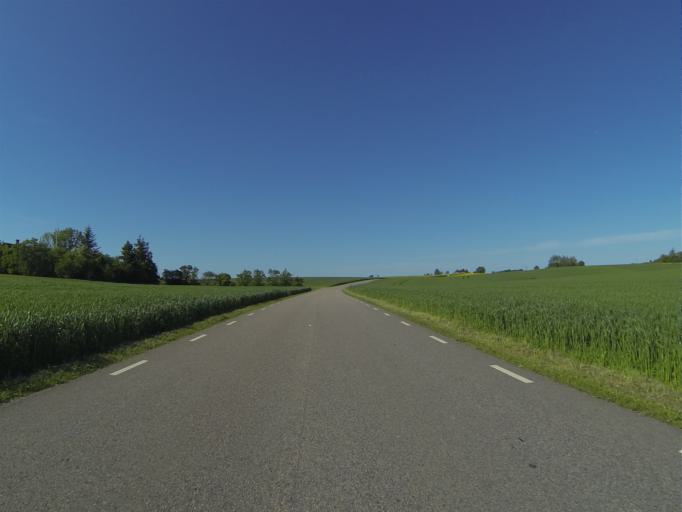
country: SE
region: Skane
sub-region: Staffanstorps Kommun
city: Hjaerup
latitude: 55.6061
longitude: 13.1412
